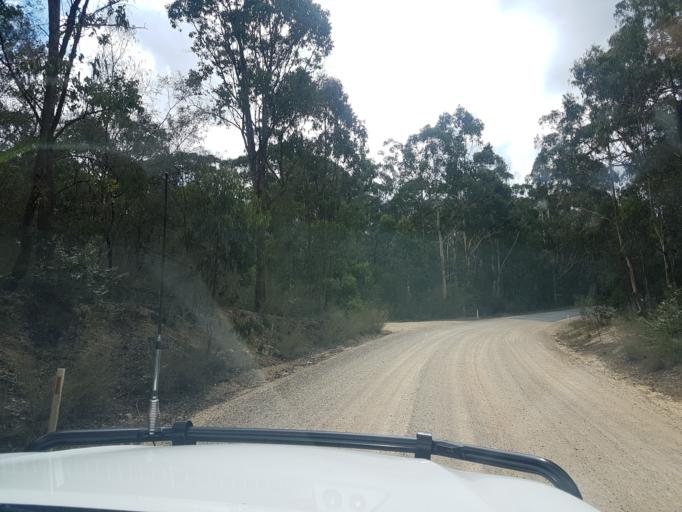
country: AU
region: Victoria
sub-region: East Gippsland
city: Bairnsdale
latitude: -37.6794
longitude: 147.5512
